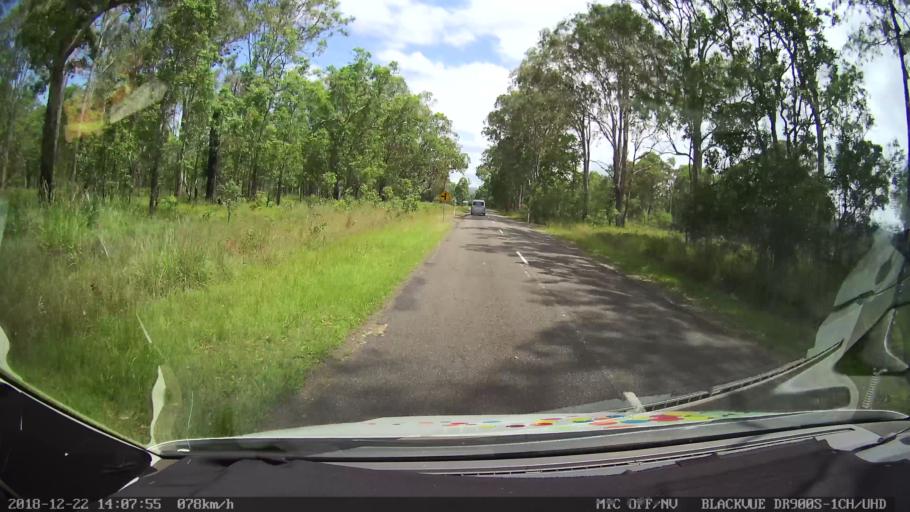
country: AU
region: New South Wales
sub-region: Clarence Valley
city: Coutts Crossing
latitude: -29.9726
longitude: 152.7262
